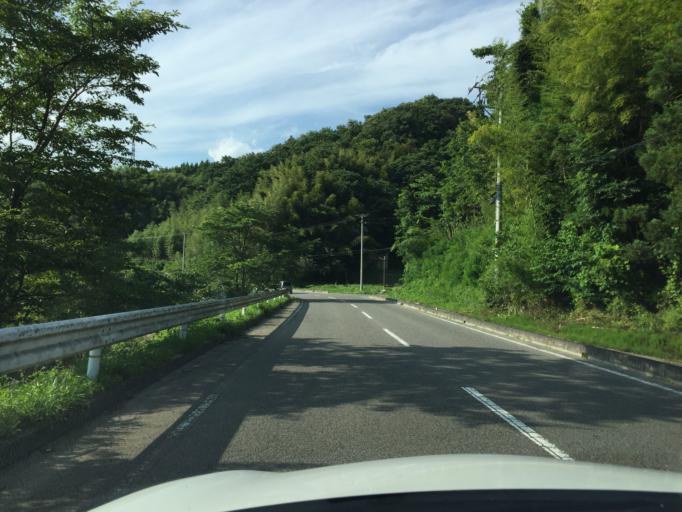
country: JP
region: Fukushima
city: Miharu
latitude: 37.3898
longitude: 140.5063
